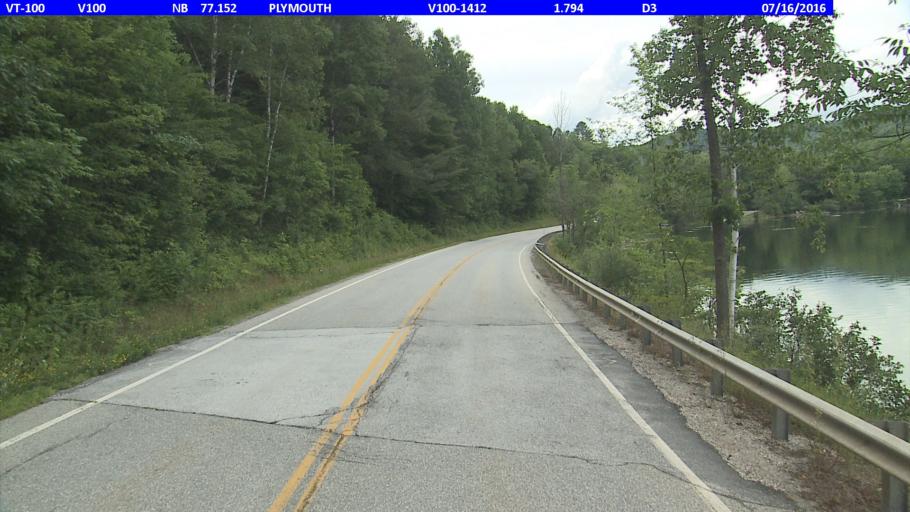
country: US
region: Vermont
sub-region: Windsor County
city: Woodstock
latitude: 43.4880
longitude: -72.7074
